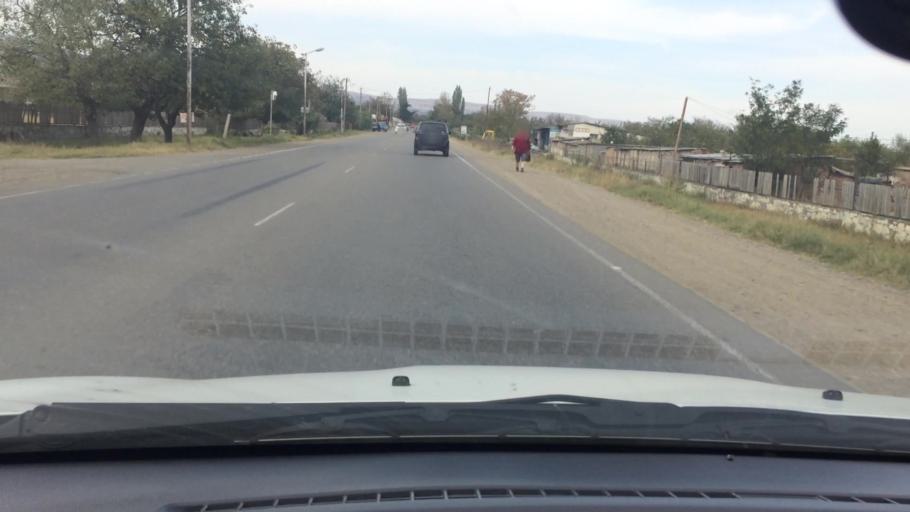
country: GE
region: Kvemo Kartli
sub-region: Marneuli
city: Marneuli
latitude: 41.5754
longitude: 44.7748
